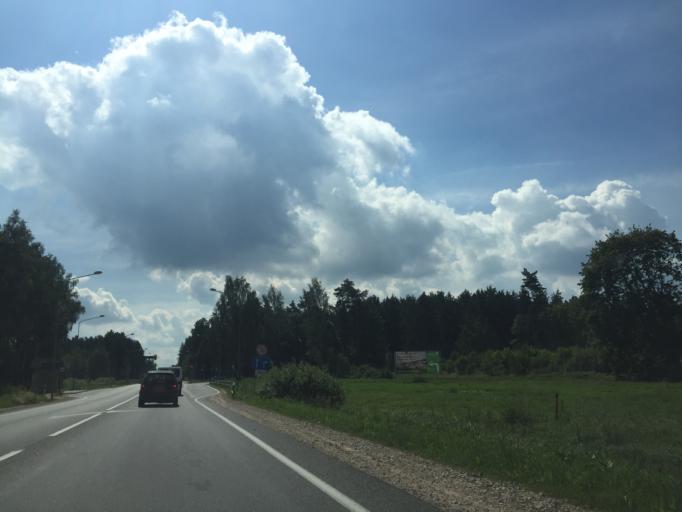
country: LV
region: Kekava
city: Balozi
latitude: 56.8862
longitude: 24.1532
